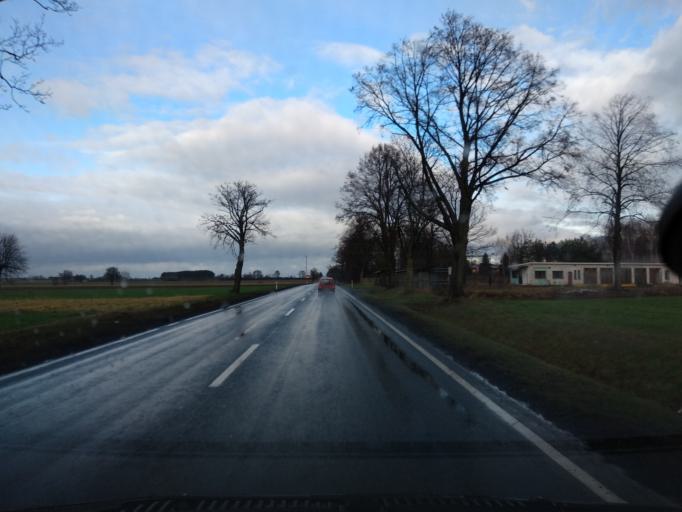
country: PL
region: Greater Poland Voivodeship
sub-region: Powiat koninski
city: Rychwal
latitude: 52.0440
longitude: 18.1622
